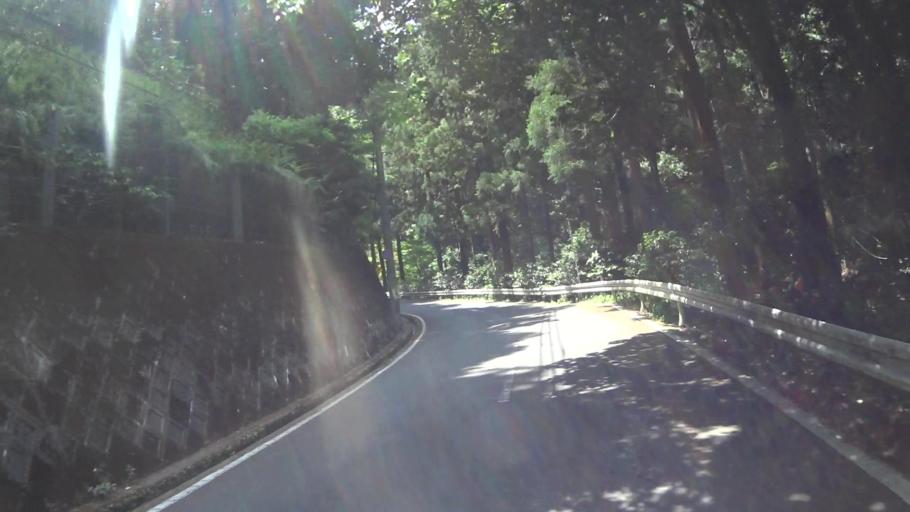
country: JP
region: Kyoto
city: Muko
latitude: 34.9405
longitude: 135.6480
